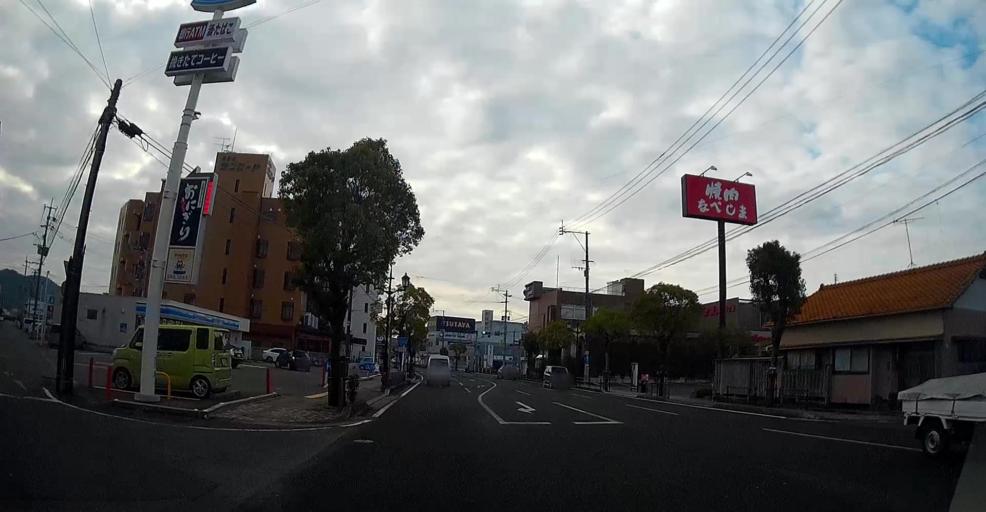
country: JP
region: Kumamoto
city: Hondo
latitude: 32.4550
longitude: 130.1942
